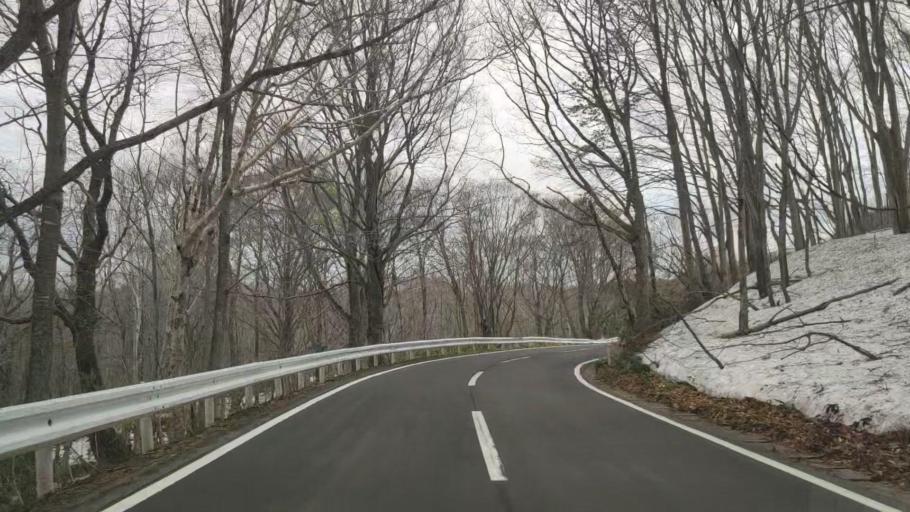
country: JP
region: Aomori
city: Aomori Shi
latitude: 40.6999
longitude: 140.9015
